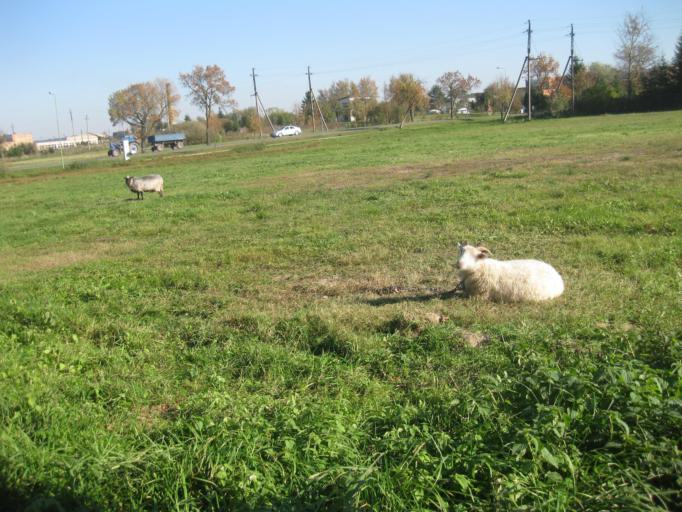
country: LT
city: Vilkija
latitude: 55.0472
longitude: 23.5724
